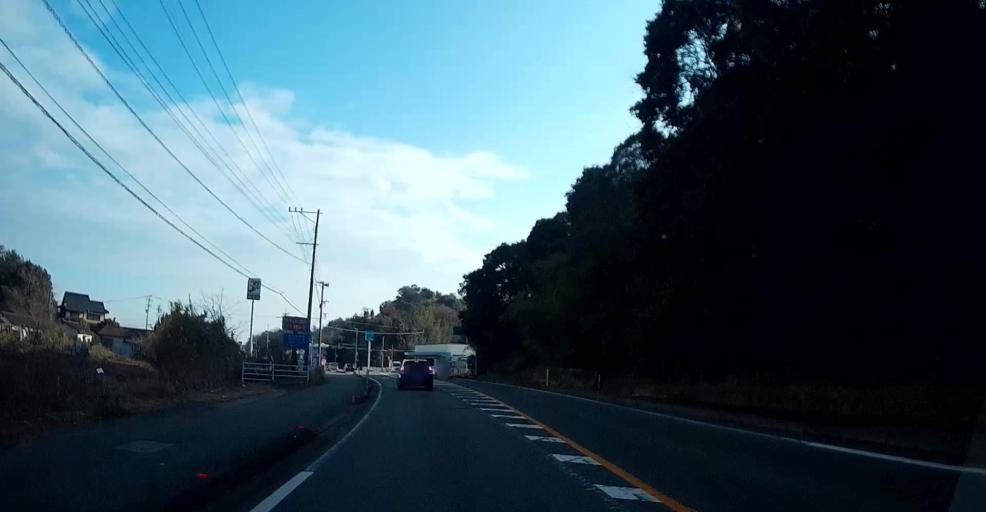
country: JP
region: Kumamoto
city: Yatsushiro
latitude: 32.5536
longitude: 130.4172
